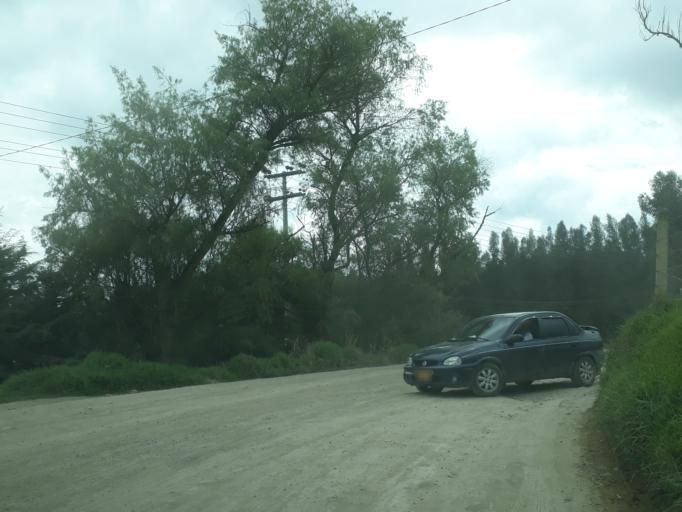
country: CO
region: Cundinamarca
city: Ubate
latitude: 5.3238
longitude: -73.7705
